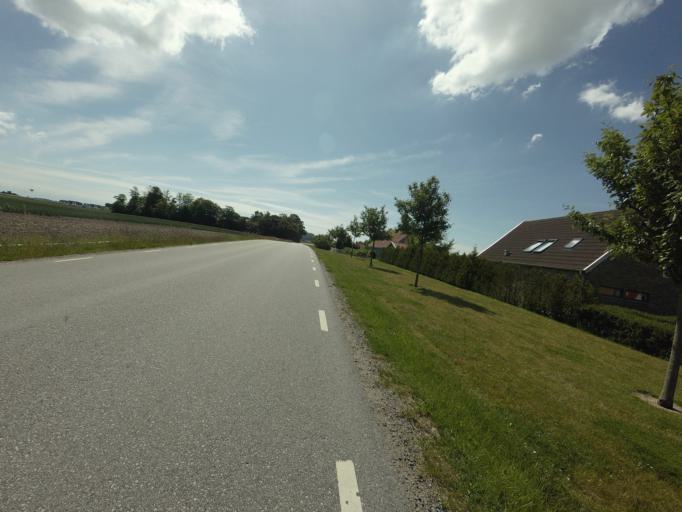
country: SE
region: Skane
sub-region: Trelleborgs Kommun
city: Skare
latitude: 55.4089
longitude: 13.0834
